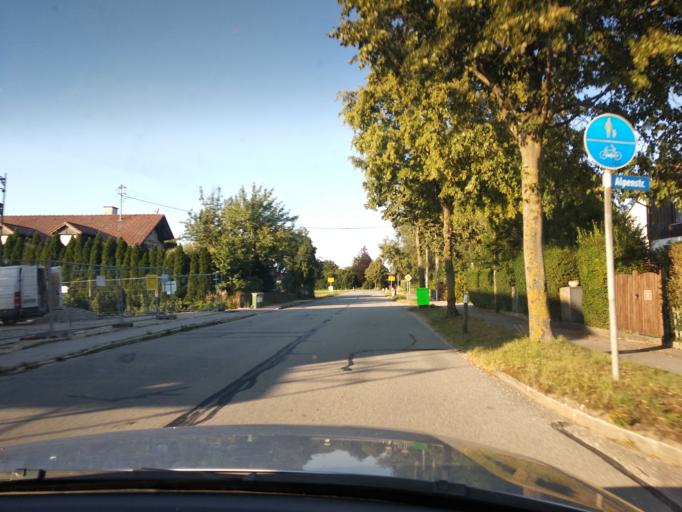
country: DE
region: Bavaria
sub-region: Upper Bavaria
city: Forstinning
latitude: 48.1609
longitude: 11.9017
